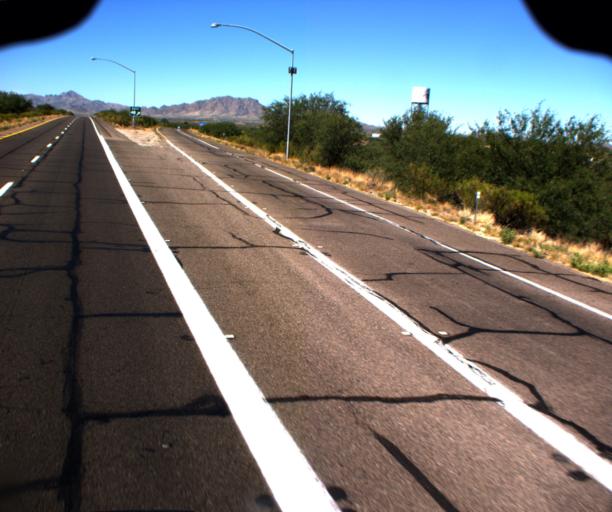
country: US
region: Arizona
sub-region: Pima County
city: Arivaca Junction
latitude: 31.7295
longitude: -111.0568
